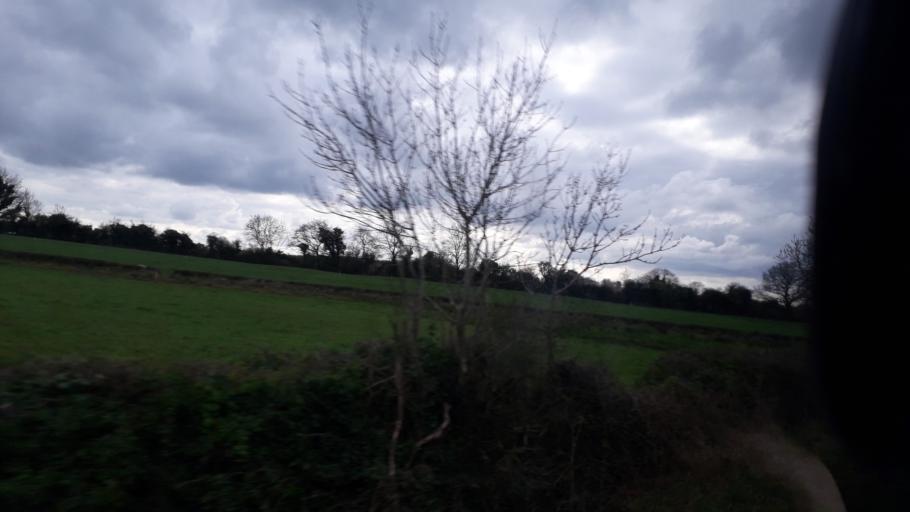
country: IE
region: Leinster
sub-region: An Longfort
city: Edgeworthstown
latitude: 53.7014
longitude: -7.6784
